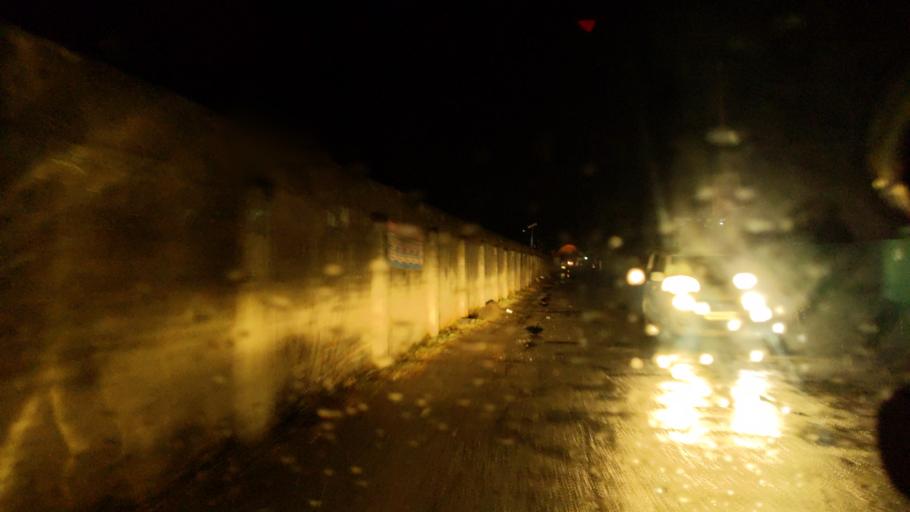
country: IN
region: Uttarakhand
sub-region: Naini Tal
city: Haldwani
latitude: 29.2069
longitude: 79.5025
